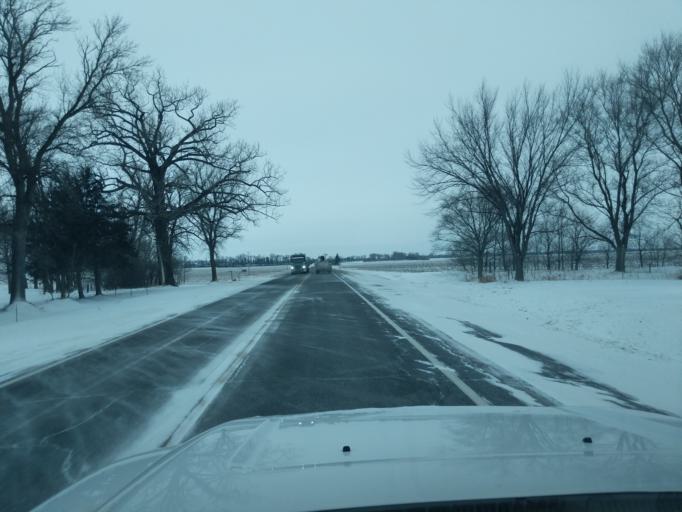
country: US
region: Minnesota
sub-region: Redwood County
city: Redwood Falls
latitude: 44.5983
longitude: -94.9944
